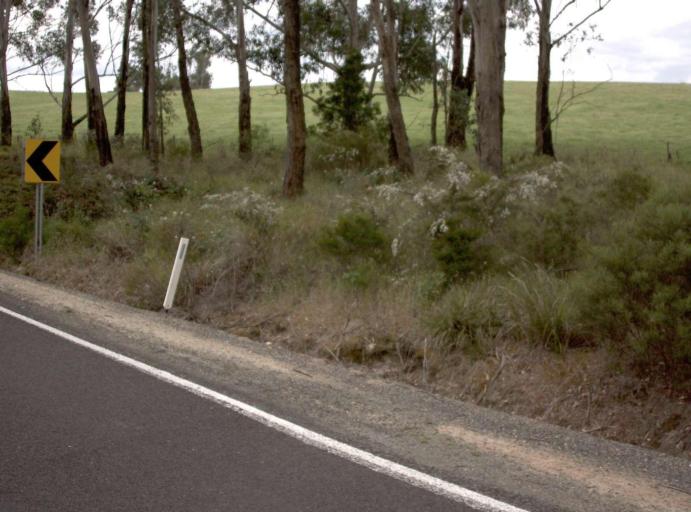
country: AU
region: New South Wales
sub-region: Bombala
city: Bombala
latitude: -37.4762
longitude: 149.1805
